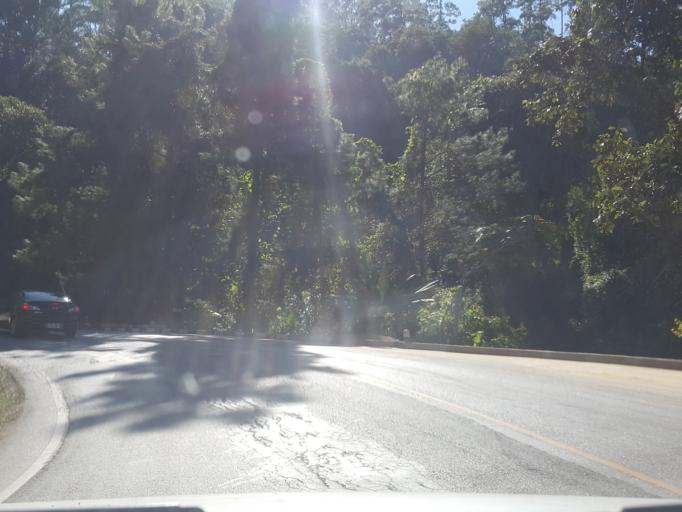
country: TH
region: Mae Hong Son
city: Mae Hi
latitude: 19.2713
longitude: 98.5453
